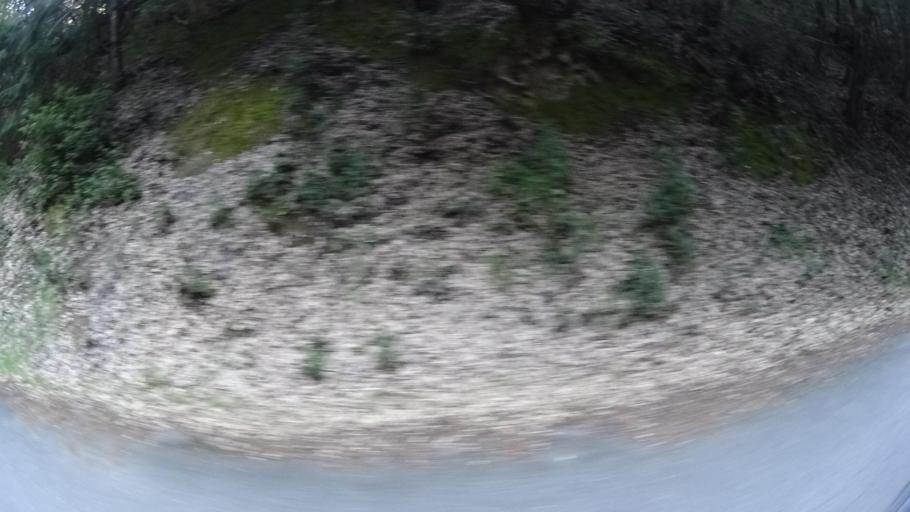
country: US
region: California
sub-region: Humboldt County
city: Blue Lake
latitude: 40.7011
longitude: -123.9408
